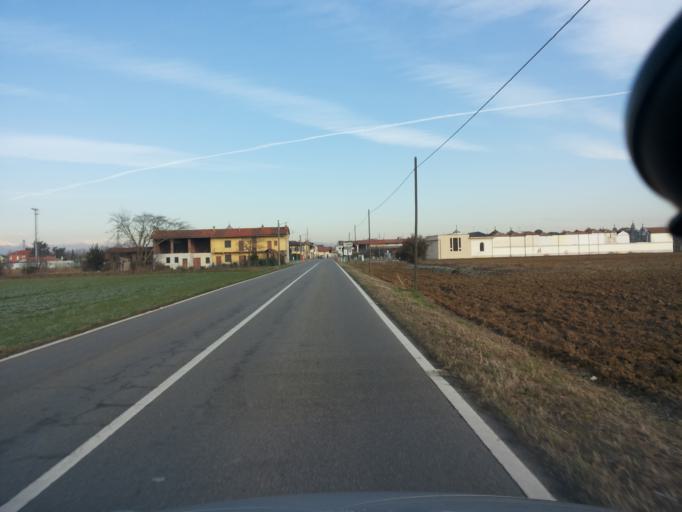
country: IT
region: Piedmont
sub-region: Provincia di Vercelli
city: Greggio
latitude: 45.4480
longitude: 8.3846
